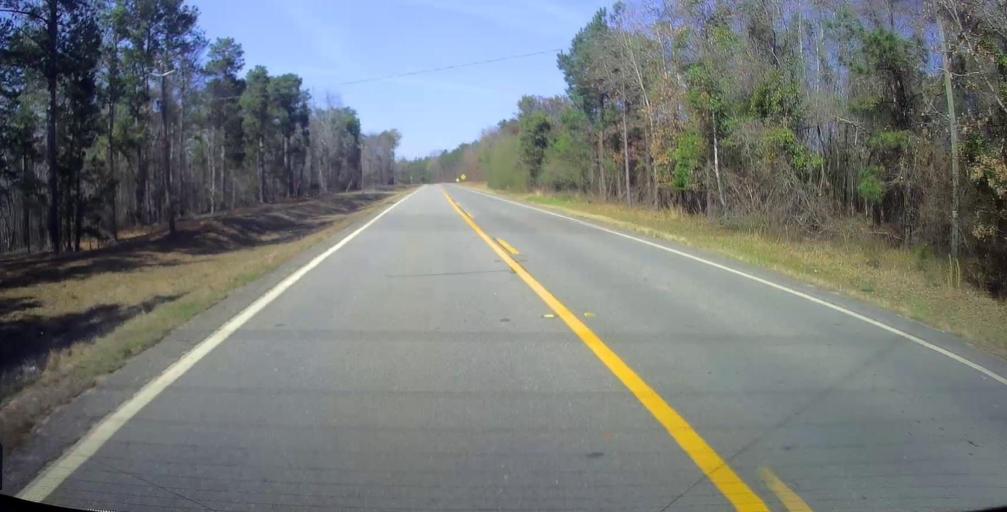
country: US
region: Georgia
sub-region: Wilkinson County
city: Gordon
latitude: 32.8355
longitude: -83.3301
